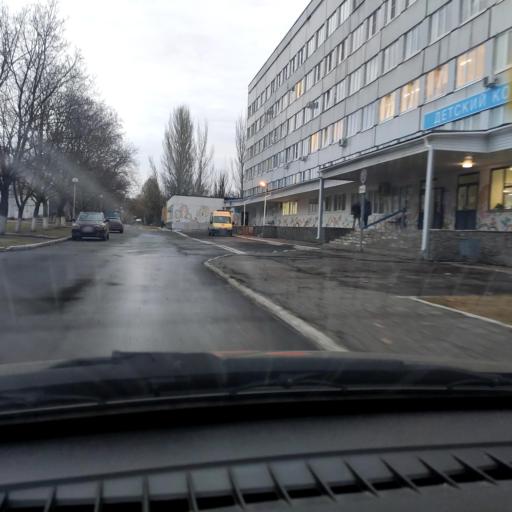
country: RU
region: Samara
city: Tol'yatti
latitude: 53.5205
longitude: 49.3192
